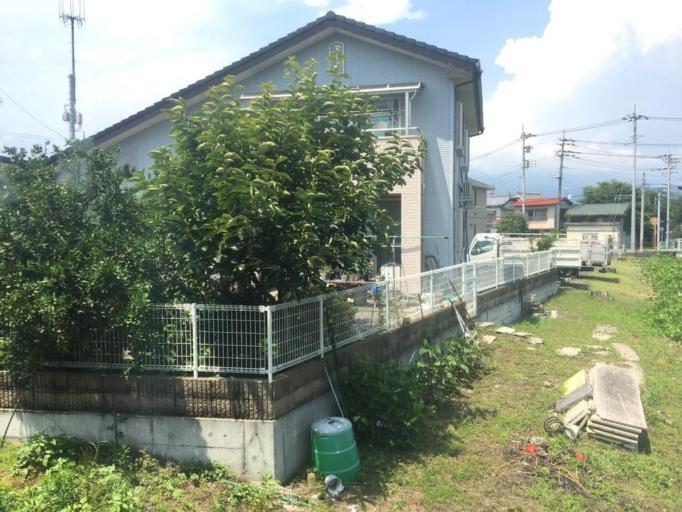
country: JP
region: Gunma
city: Maebashi-shi
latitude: 36.4131
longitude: 139.1580
